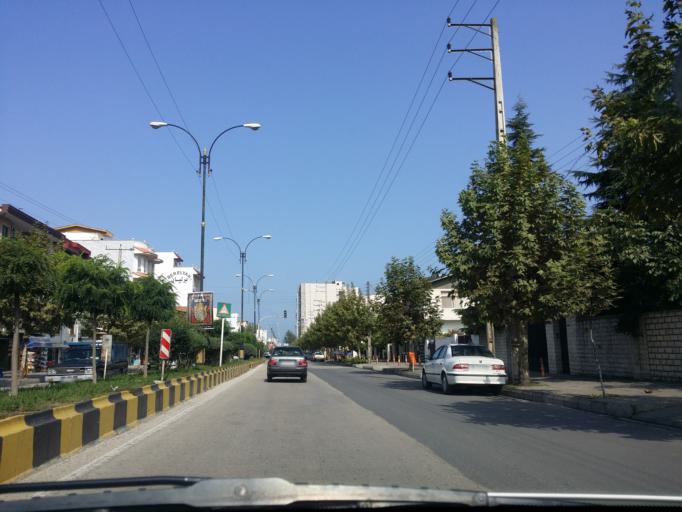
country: IR
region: Mazandaran
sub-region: Nowshahr
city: Nowshahr
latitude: 36.6425
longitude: 51.4911
